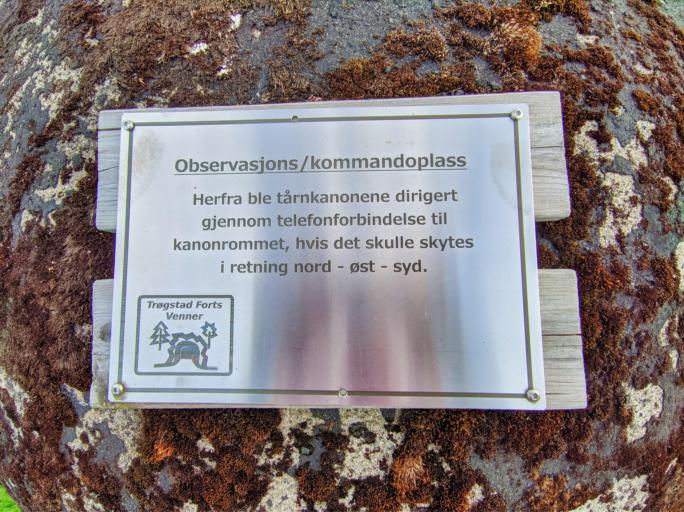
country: NO
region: Ostfold
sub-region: Trogstad
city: Skjonhaug
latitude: 59.6322
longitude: 11.3466
